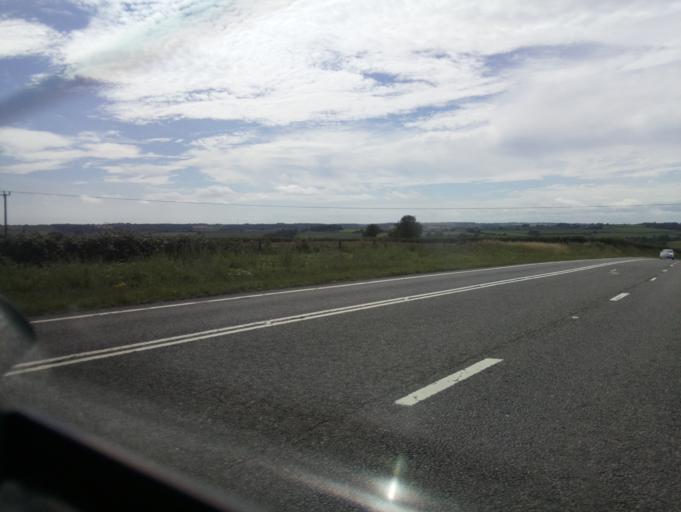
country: GB
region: England
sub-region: Dorset
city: Sherborne
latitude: 50.8277
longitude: -2.5663
